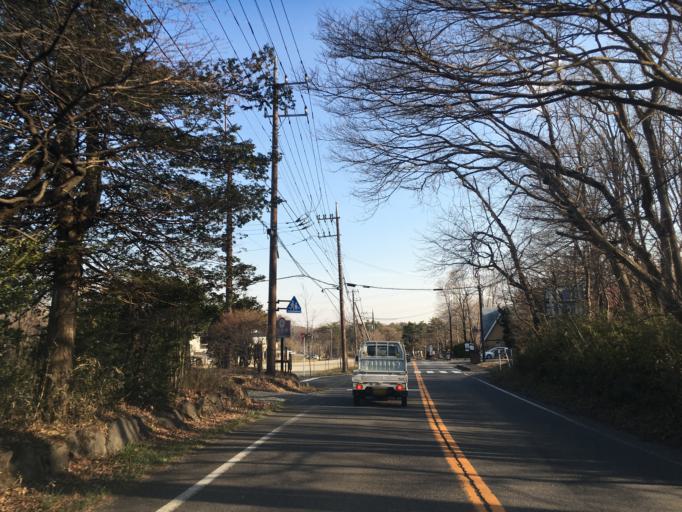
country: JP
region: Tochigi
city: Kuroiso
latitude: 37.0332
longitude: 140.0205
